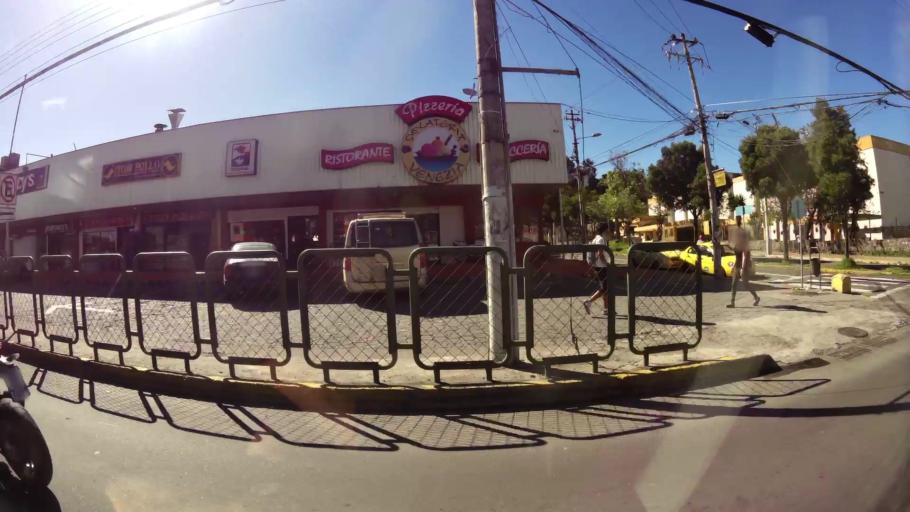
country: EC
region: Pichincha
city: Quito
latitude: -0.1745
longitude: -78.4771
